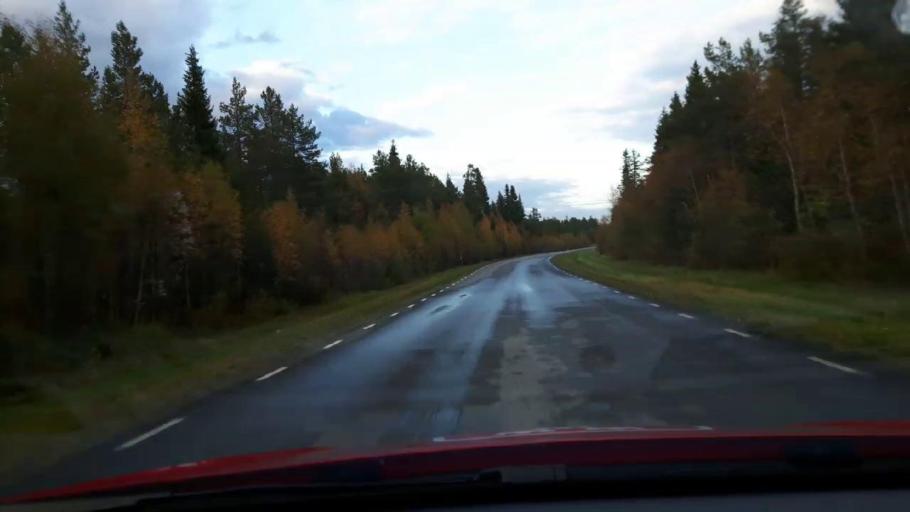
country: SE
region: Jaemtland
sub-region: OEstersunds Kommun
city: Lit
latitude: 63.3104
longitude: 15.0096
